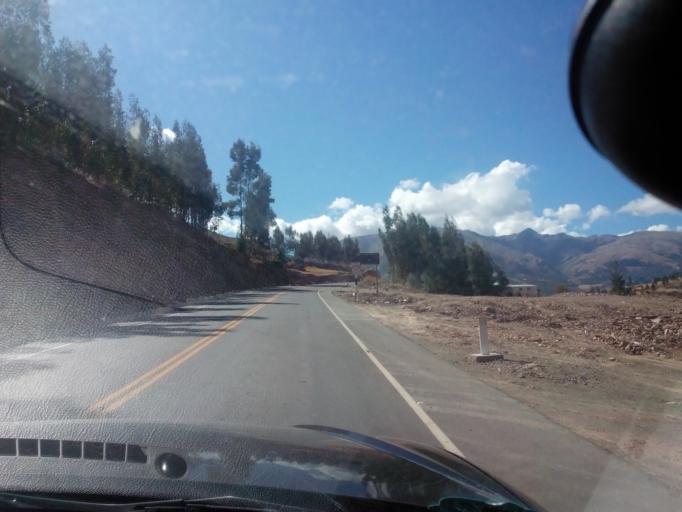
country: PE
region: Cusco
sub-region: Provincia de Quispicanchis
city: Urcos
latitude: -13.6853
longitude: -71.6294
